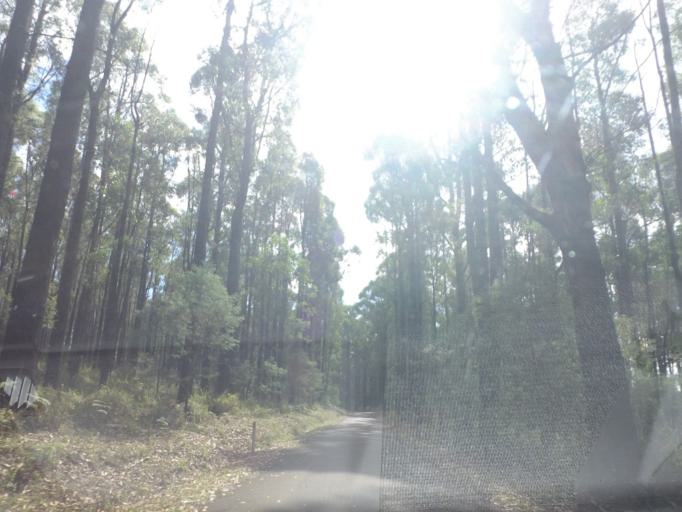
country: AU
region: Victoria
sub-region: Yarra Ranges
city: Healesville
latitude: -37.5638
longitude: 145.6833
